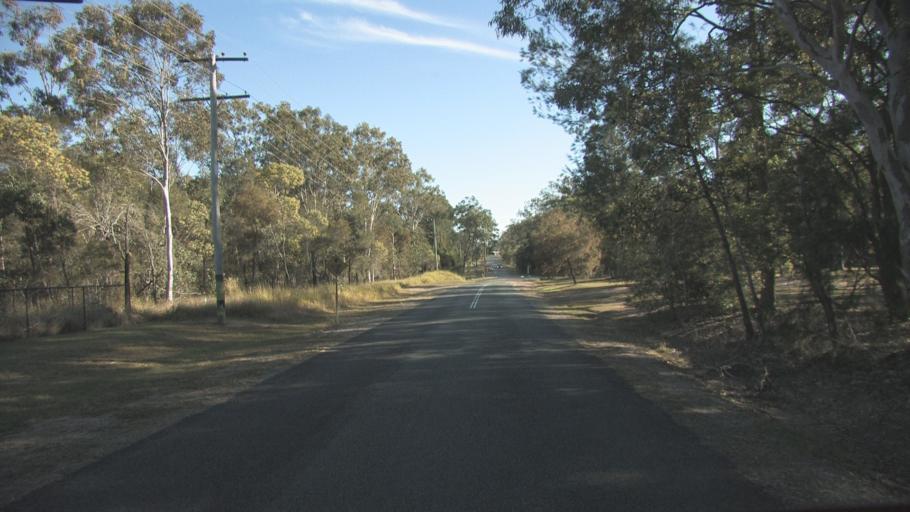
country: AU
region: Queensland
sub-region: Logan
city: Park Ridge South
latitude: -27.7191
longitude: 152.9814
